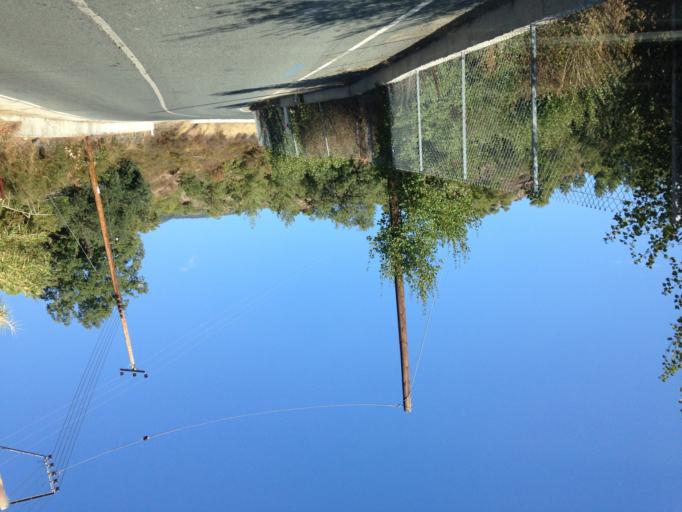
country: CY
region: Limassol
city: Pachna
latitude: 34.8820
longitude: 32.8410
